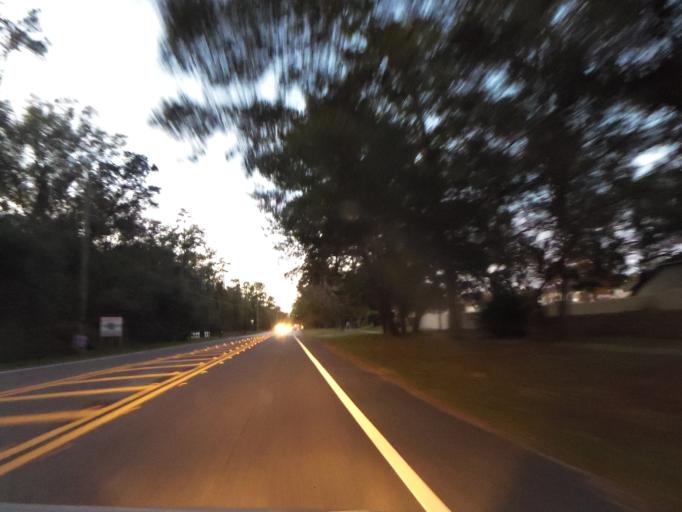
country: US
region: Florida
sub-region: Saint Johns County
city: Saint Augustine Shores
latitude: 29.8178
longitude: -81.3448
